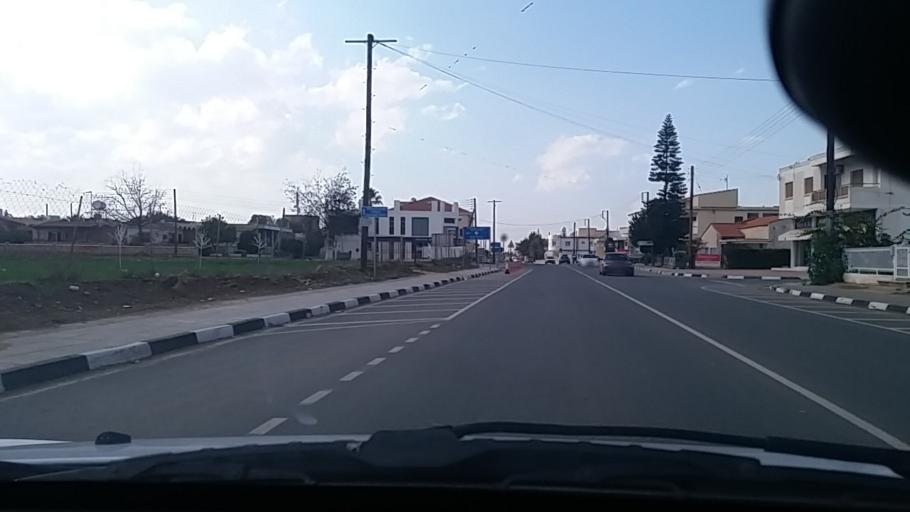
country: CY
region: Lefkosia
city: Kokkinotrimithia
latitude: 35.1487
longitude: 33.2020
